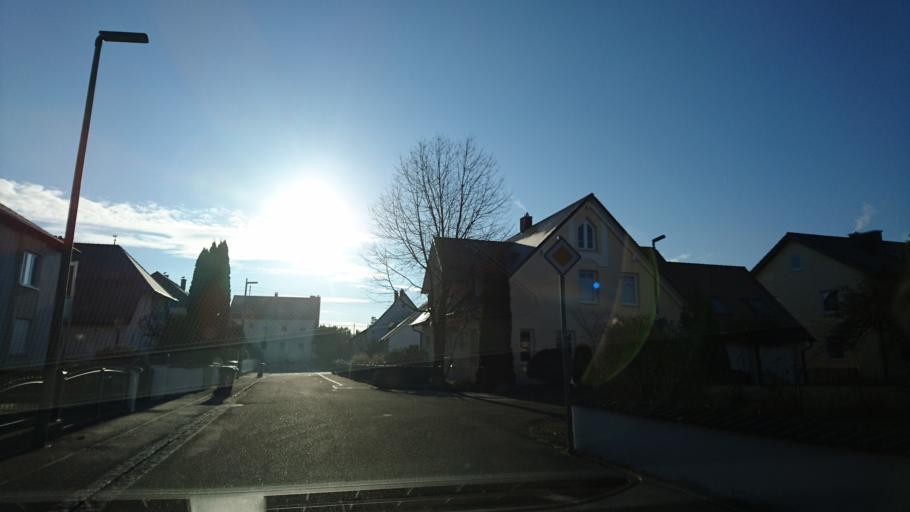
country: DE
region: Bavaria
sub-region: Swabia
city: Nordendorf
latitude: 48.5970
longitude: 10.8347
